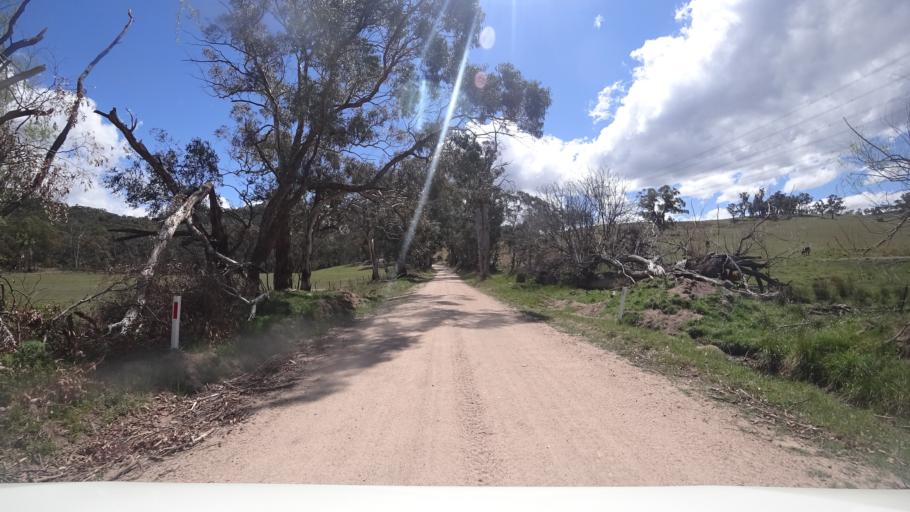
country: AU
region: New South Wales
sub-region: Oberon
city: Oberon
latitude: -33.5531
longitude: 149.9319
